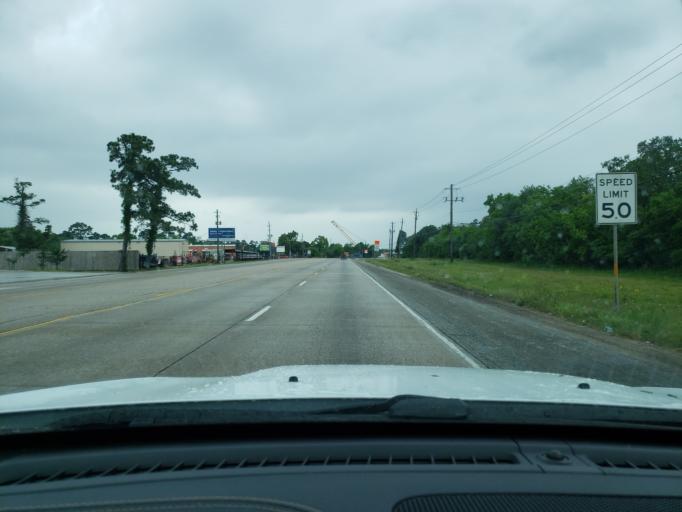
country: US
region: Texas
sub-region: Chambers County
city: Mont Belvieu
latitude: 29.7772
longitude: -94.9135
